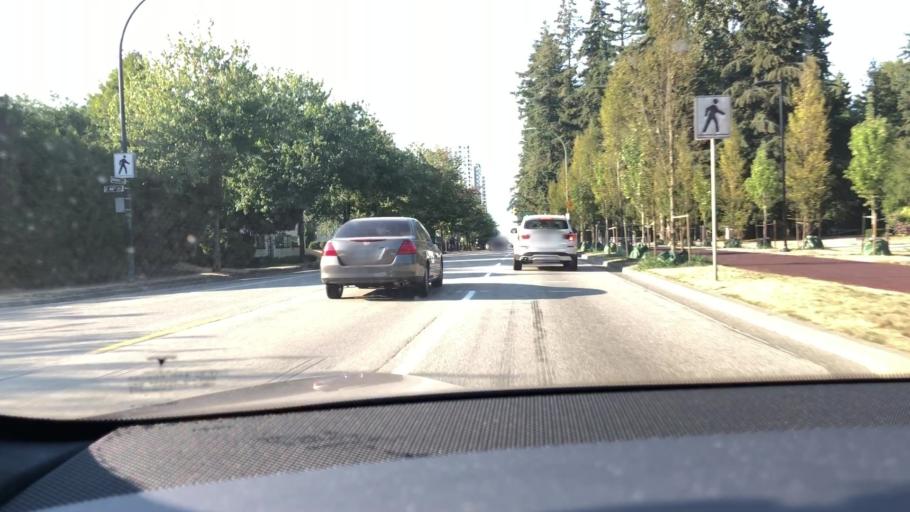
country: CA
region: British Columbia
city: Burnaby
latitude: 49.2280
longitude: -123.0235
